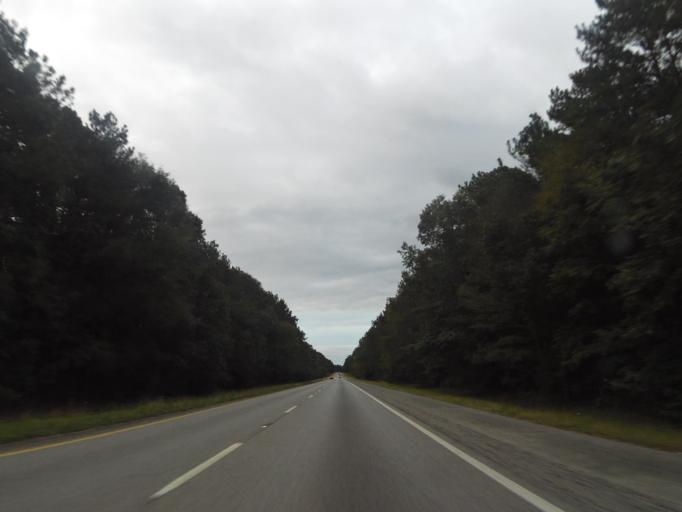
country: US
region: Alabama
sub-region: Saint Clair County
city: Ashville
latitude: 33.8377
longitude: -86.3260
